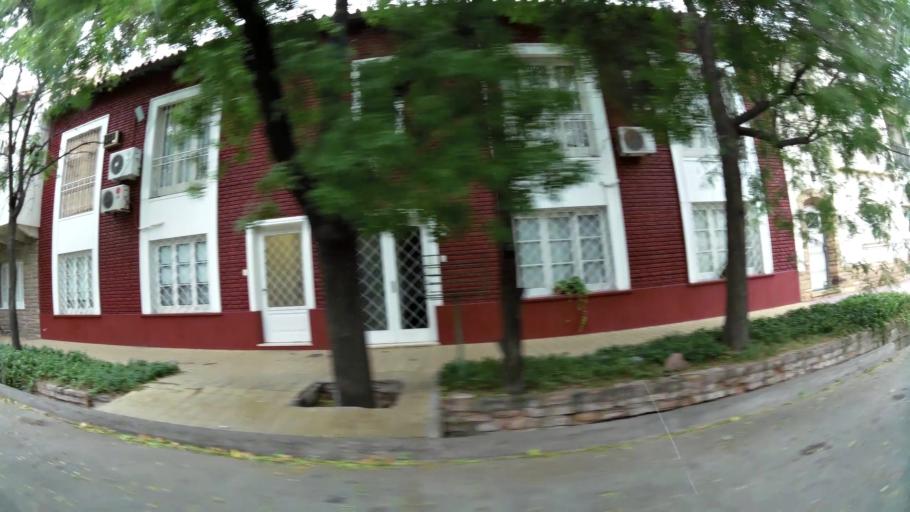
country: AR
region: Mendoza
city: Mendoza
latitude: -32.8886
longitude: -68.8558
